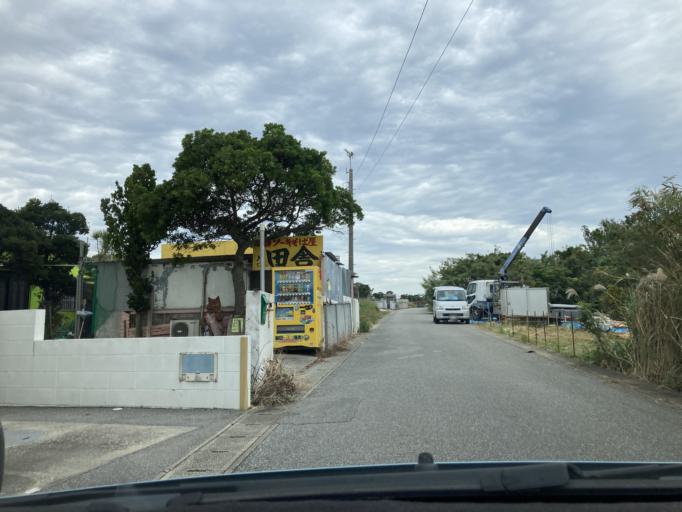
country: JP
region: Okinawa
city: Ishikawa
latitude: 26.4057
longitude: 127.7393
